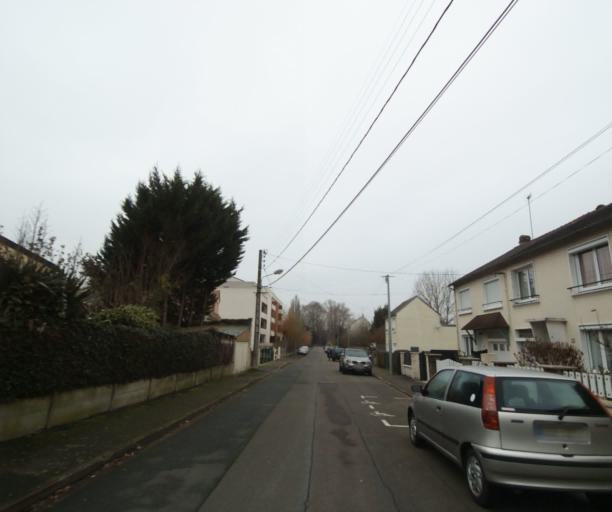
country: FR
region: Pays de la Loire
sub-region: Departement de la Sarthe
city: Le Mans
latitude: 47.9844
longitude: 0.2011
